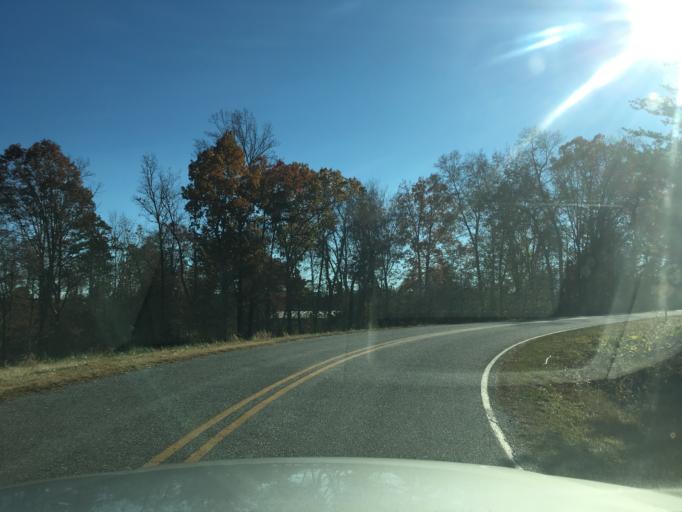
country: US
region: North Carolina
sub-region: Rutherford County
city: Rutherfordton
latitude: 35.2523
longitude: -82.0429
